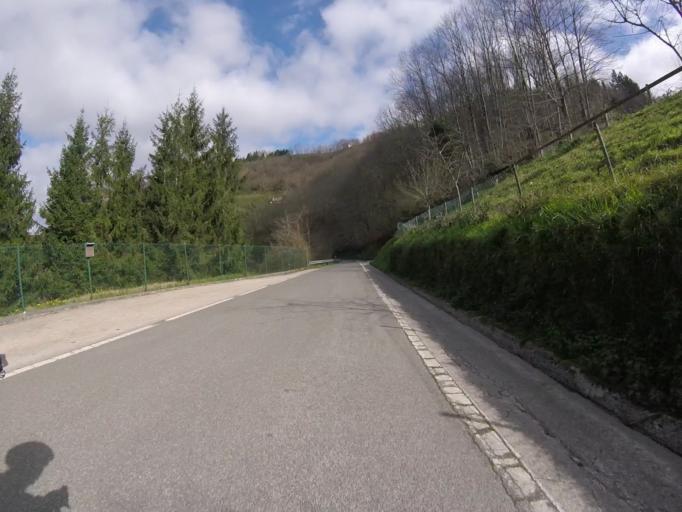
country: ES
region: Navarre
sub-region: Provincia de Navarra
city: Goizueta
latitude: 43.1664
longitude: -1.8584
